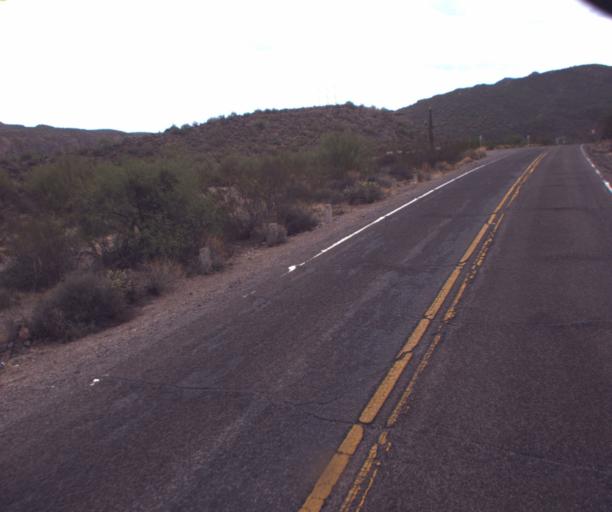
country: US
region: Arizona
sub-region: Pinal County
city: Apache Junction
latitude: 33.5341
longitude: -111.4298
